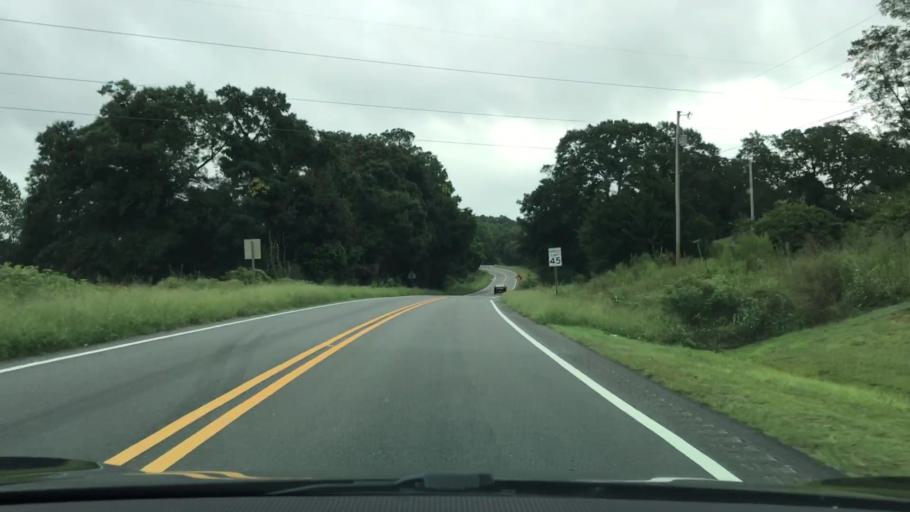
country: US
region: Alabama
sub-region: Covington County
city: Opp
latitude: 31.2173
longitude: -86.1657
